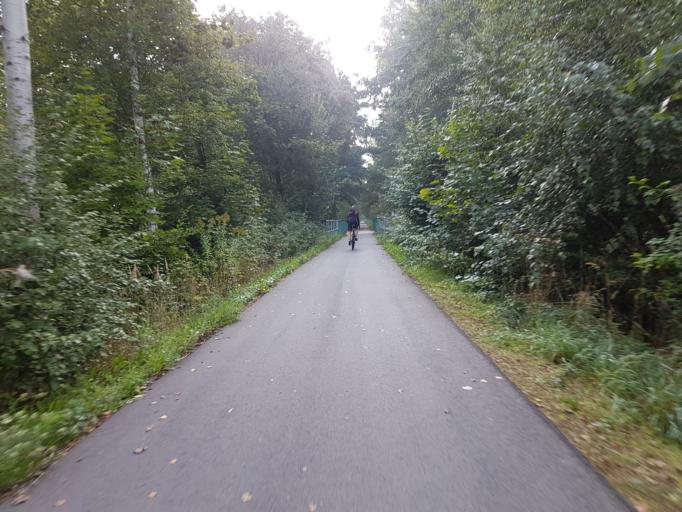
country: DE
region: Saxony
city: Claussnitz
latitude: 50.9145
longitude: 12.8890
